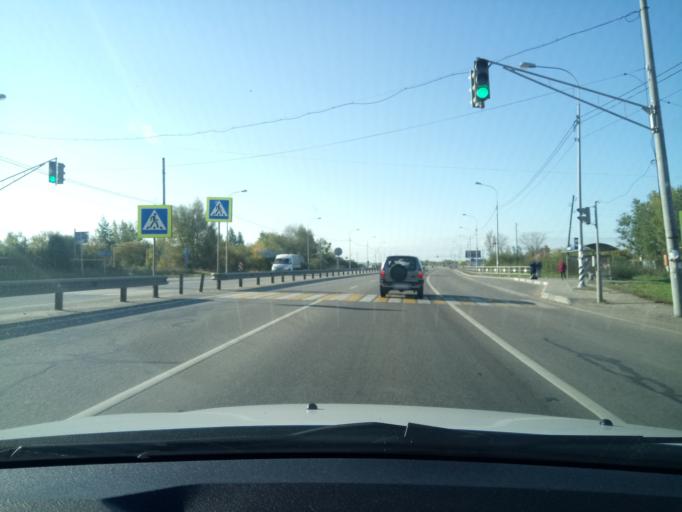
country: RU
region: Nizjnij Novgorod
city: Burevestnik
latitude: 56.1634
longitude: 43.9156
